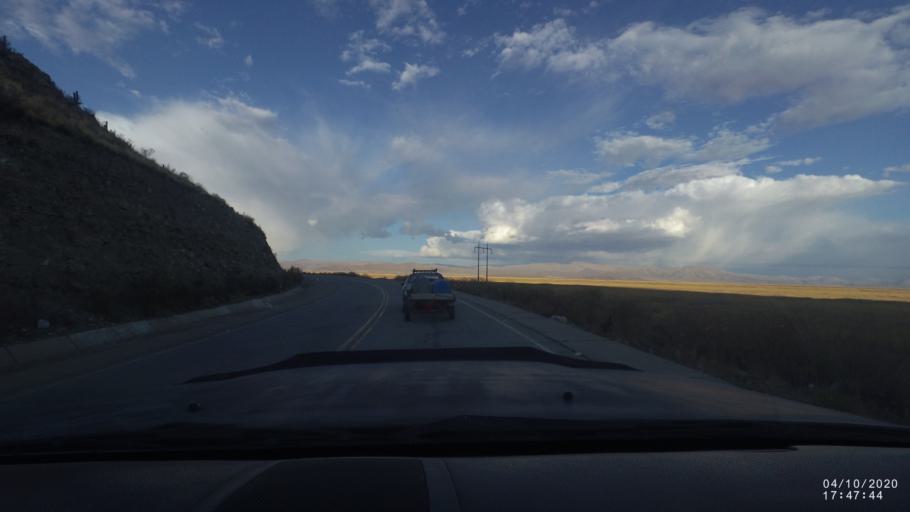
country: BO
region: Oruro
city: Oruro
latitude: -18.0228
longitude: -67.1414
